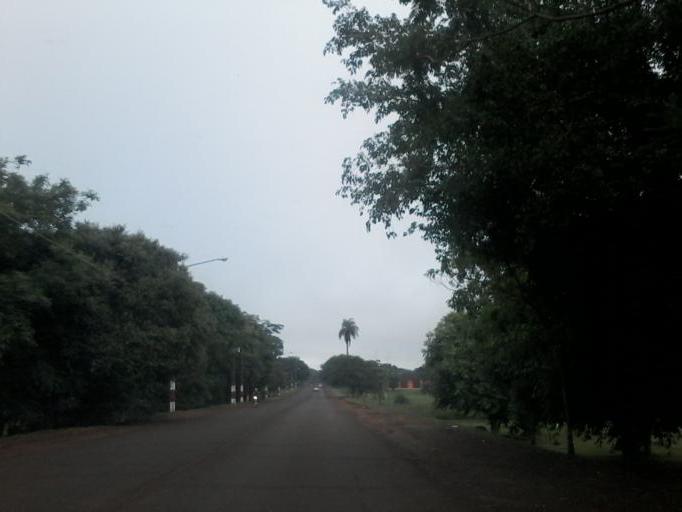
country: PY
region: Alto Parana
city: Ciudad del Este
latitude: -25.4120
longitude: -54.6267
